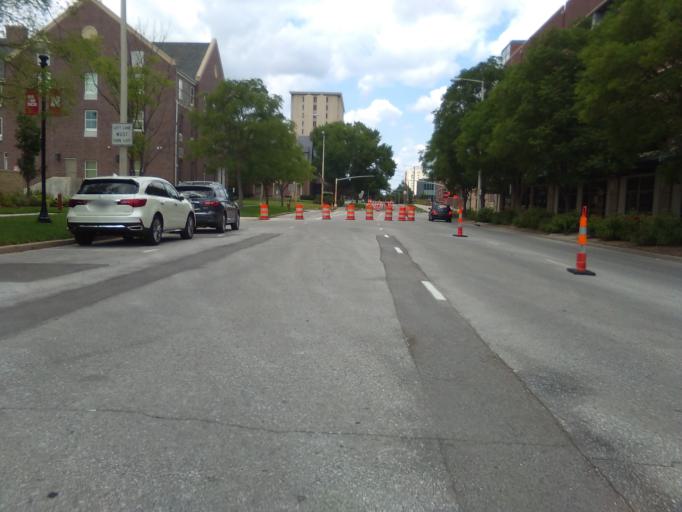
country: US
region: Nebraska
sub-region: Lancaster County
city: Lincoln
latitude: 40.8160
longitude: -96.6967
